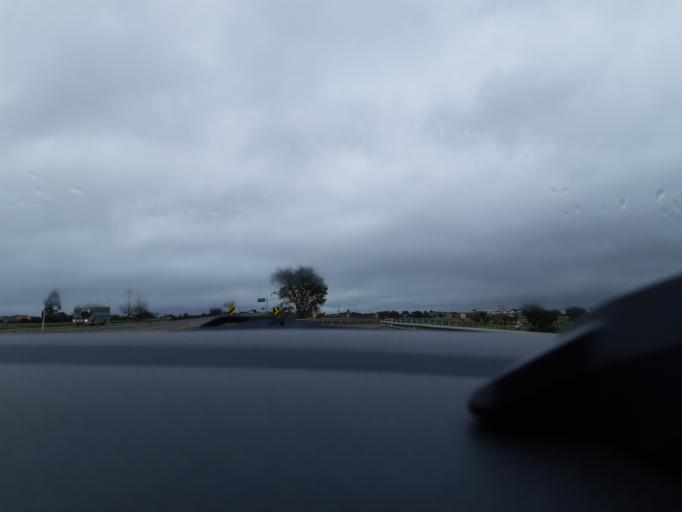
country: BR
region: Sao Paulo
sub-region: Ourinhos
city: Ourinhos
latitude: -22.9772
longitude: -49.9030
